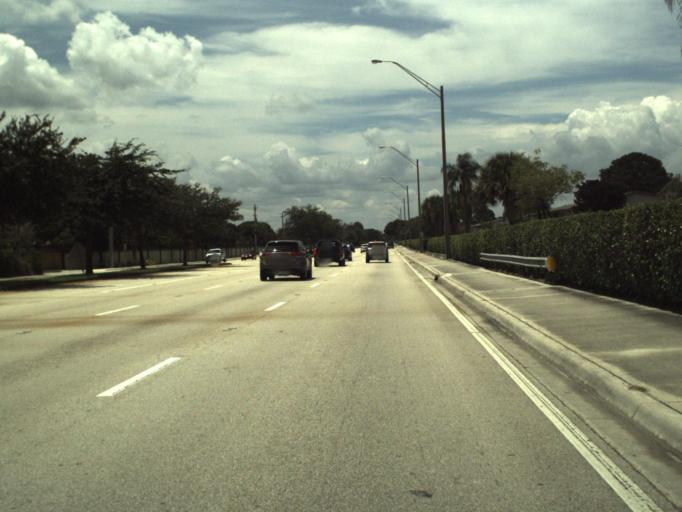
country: US
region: Florida
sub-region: Broward County
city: North Lauderdale
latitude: 26.2356
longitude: -80.2276
